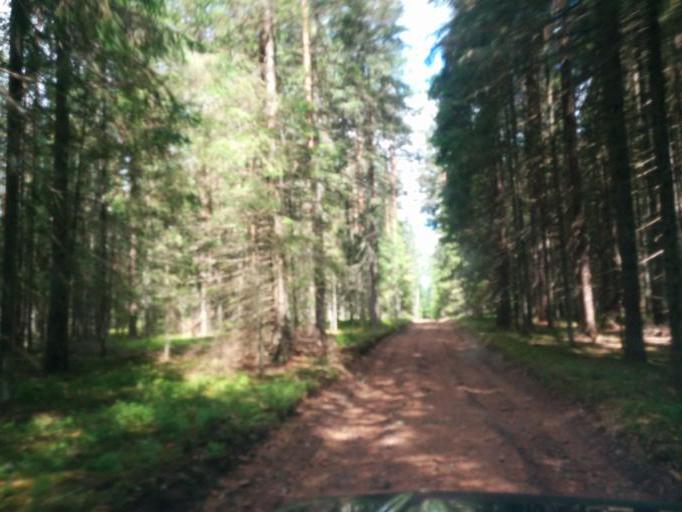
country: LV
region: Vilaka
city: Vilaka
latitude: 57.3345
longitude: 27.6925
